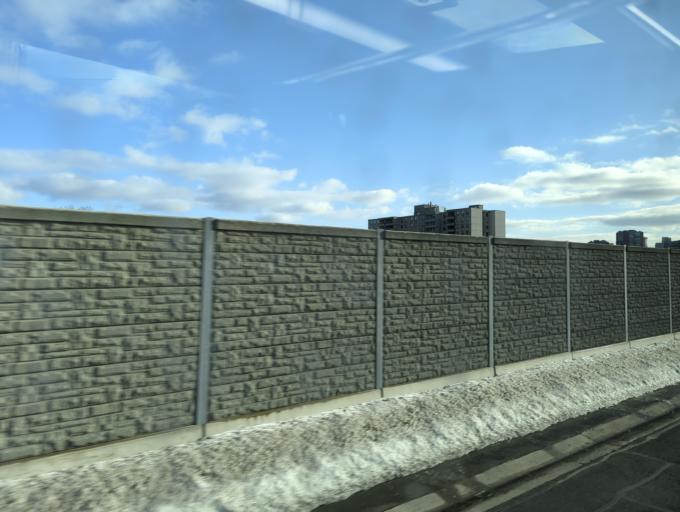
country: CA
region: Ontario
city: Mississauga
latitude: 43.6090
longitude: -79.6339
